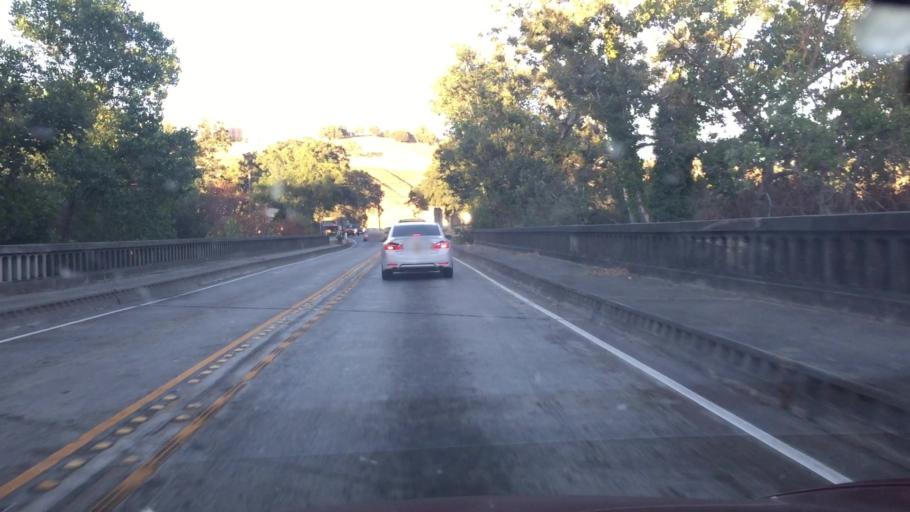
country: US
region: California
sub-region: Alameda County
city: Pleasanton
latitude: 37.5927
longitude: -121.8839
